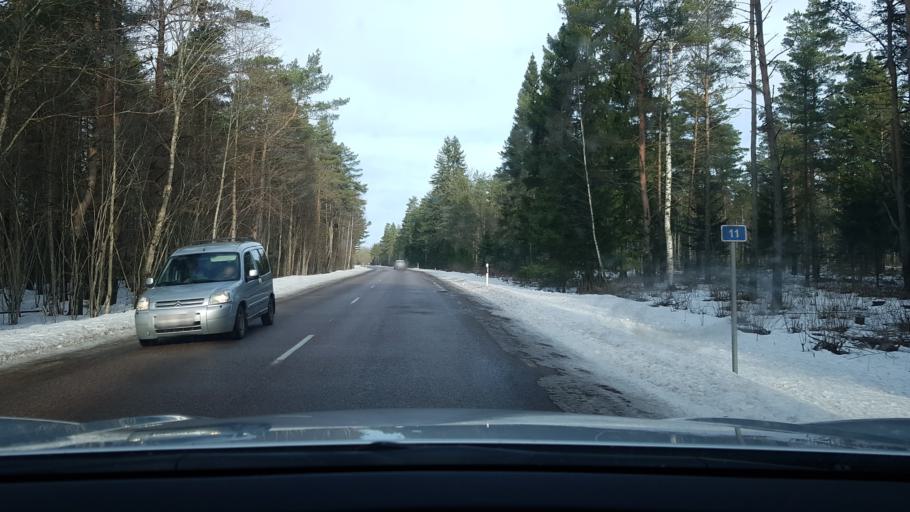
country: EE
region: Saare
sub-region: Kuressaare linn
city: Kuressaare
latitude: 58.3667
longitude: 22.6164
